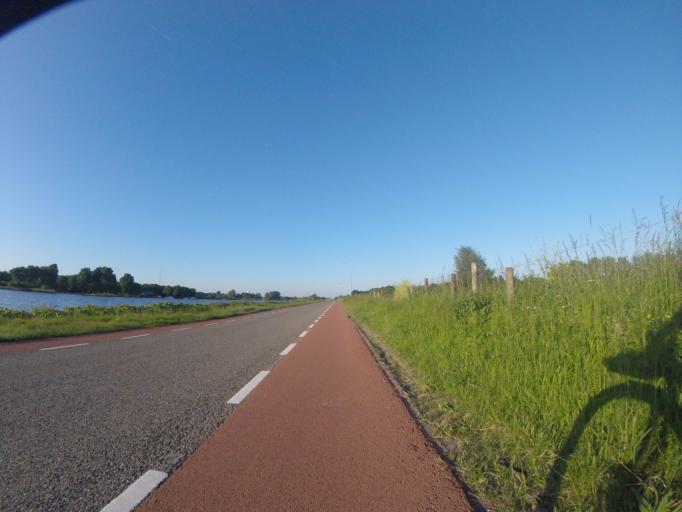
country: NL
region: North Holland
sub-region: Gemeente Heemstede
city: Heemstede
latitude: 52.3424
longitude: 4.6549
